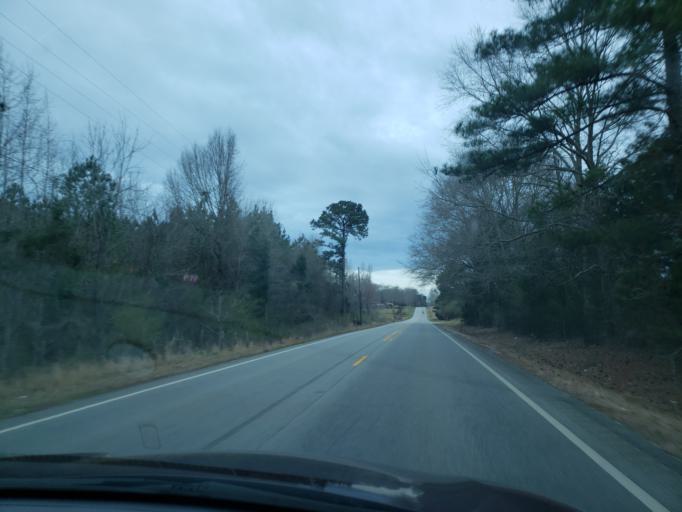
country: US
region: Alabama
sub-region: Chambers County
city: Lafayette
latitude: 32.9748
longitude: -85.4032
